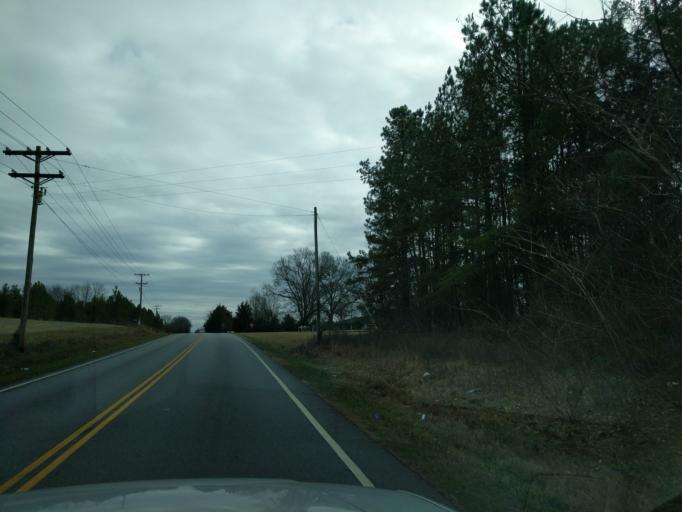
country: US
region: South Carolina
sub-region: Oconee County
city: Westminster
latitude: 34.6134
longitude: -83.0418
